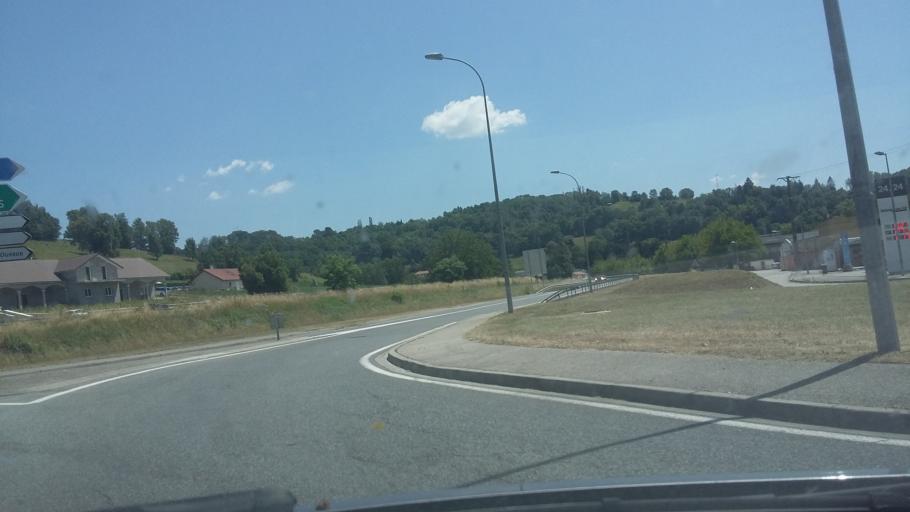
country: FR
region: Rhone-Alpes
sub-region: Departement de l'Ain
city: Belley
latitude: 45.7786
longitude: 5.6895
